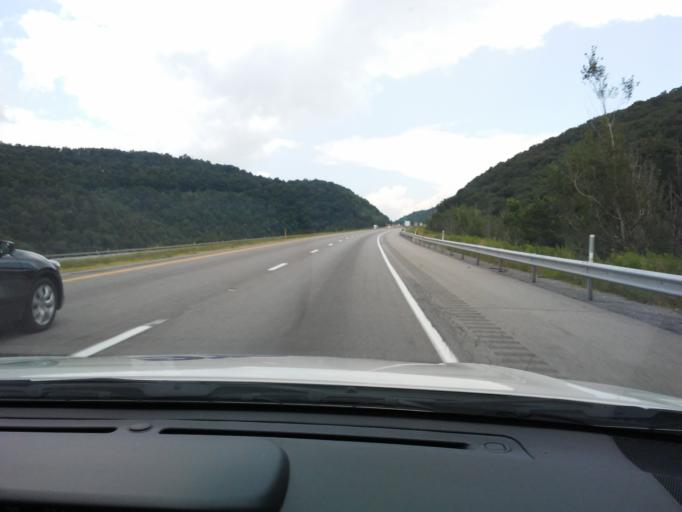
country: US
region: Pennsylvania
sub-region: Centre County
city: Milesburg
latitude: 40.9983
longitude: -77.8568
